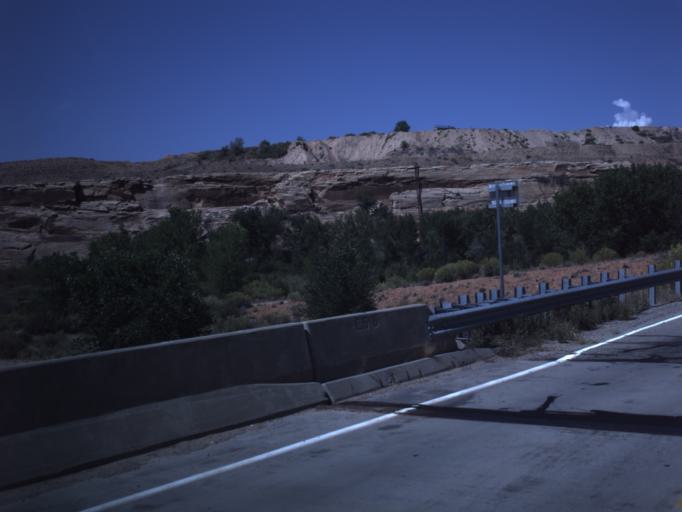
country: US
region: Utah
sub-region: San Juan County
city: Blanding
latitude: 37.2582
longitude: -109.6193
